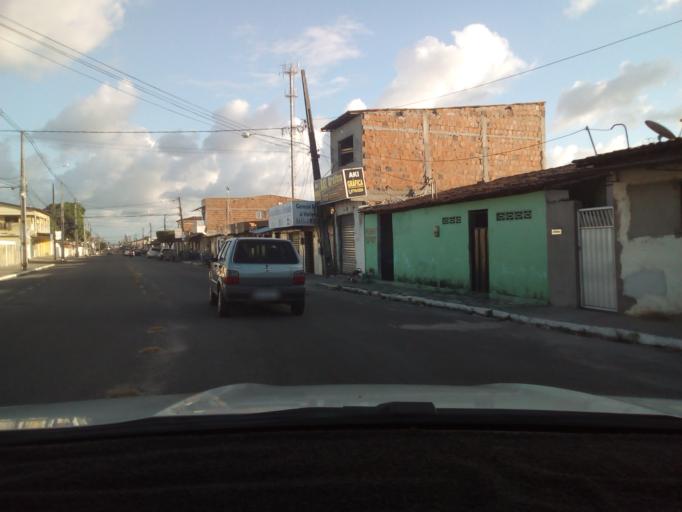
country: BR
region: Paraiba
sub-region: Joao Pessoa
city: Joao Pessoa
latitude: -7.1818
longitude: -34.8390
